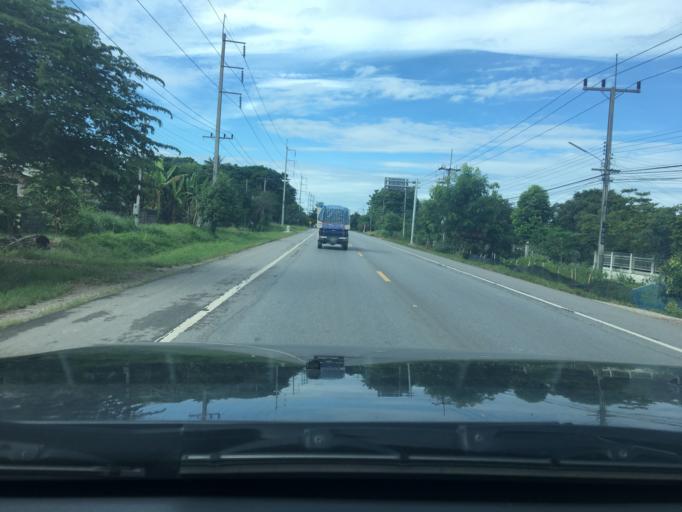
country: TH
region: Chiang Rai
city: Mae Suai
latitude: 19.6038
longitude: 99.5084
